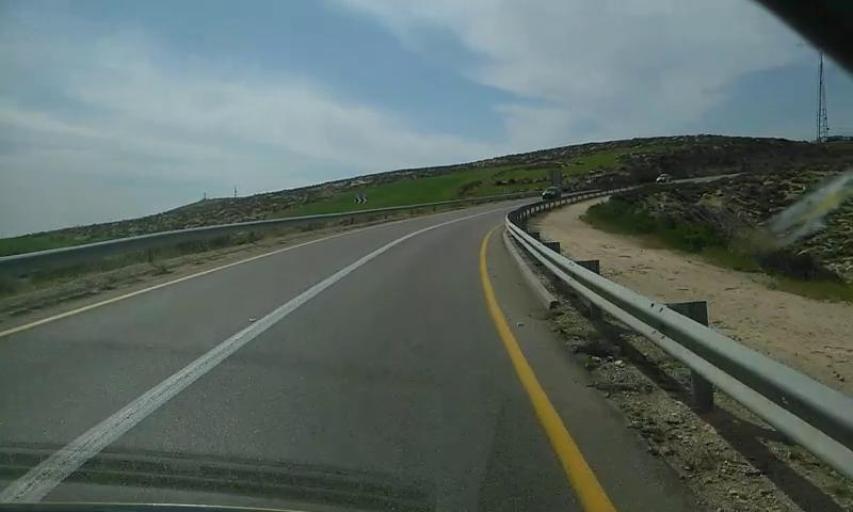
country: PS
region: West Bank
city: Az Zahiriyah
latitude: 31.3738
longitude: 35.0122
